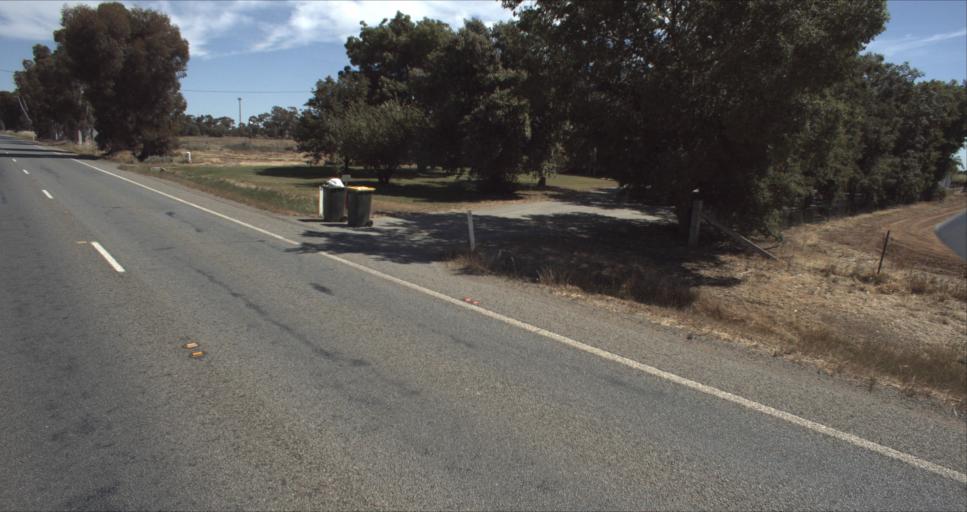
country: AU
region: New South Wales
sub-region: Leeton
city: Leeton
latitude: -34.5864
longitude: 146.4145
